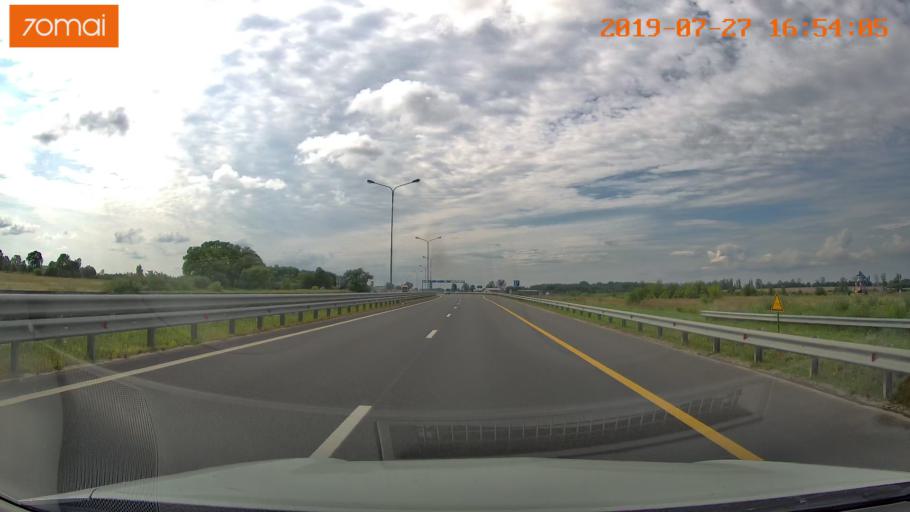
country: RU
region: Kaliningrad
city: Bol'shoe Isakovo
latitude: 54.6926
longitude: 20.8159
